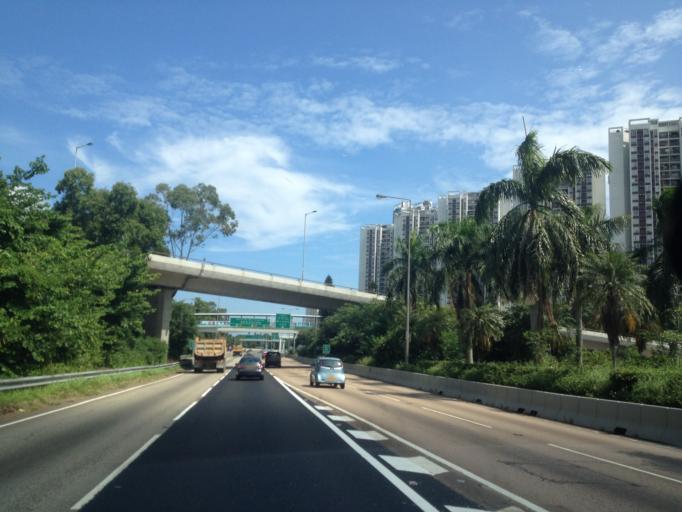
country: HK
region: Kowloon City
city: Kowloon
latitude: 22.2892
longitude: 114.2171
